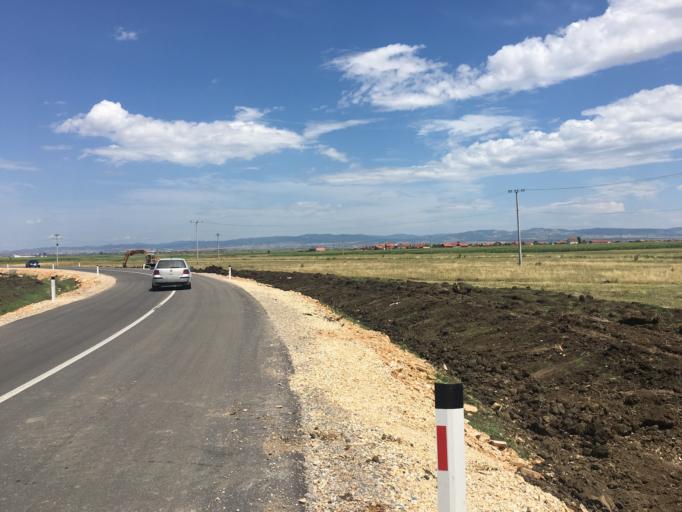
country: XK
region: Pristina
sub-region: Komuna e Gracanices
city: Glanica
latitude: 42.5448
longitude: 21.0200
